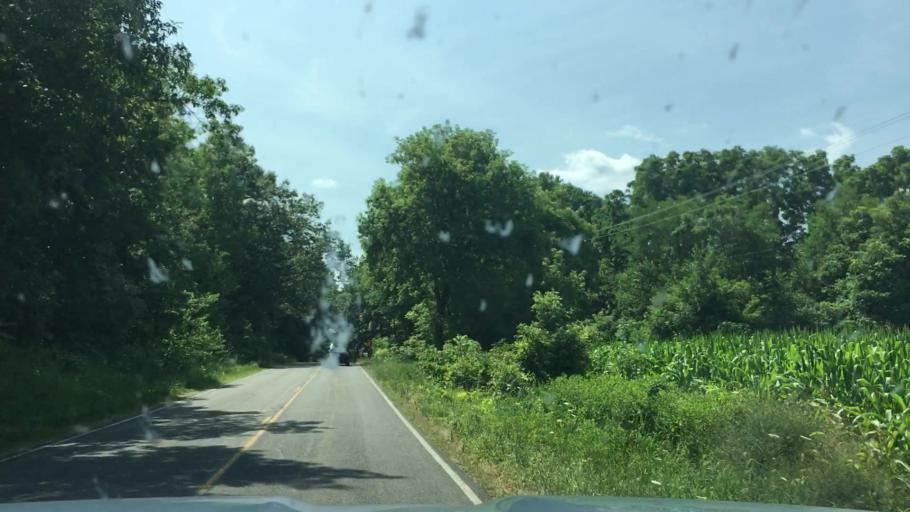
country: US
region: Michigan
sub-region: Kalamazoo County
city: Comstock Northwest
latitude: 42.4287
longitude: -85.5199
